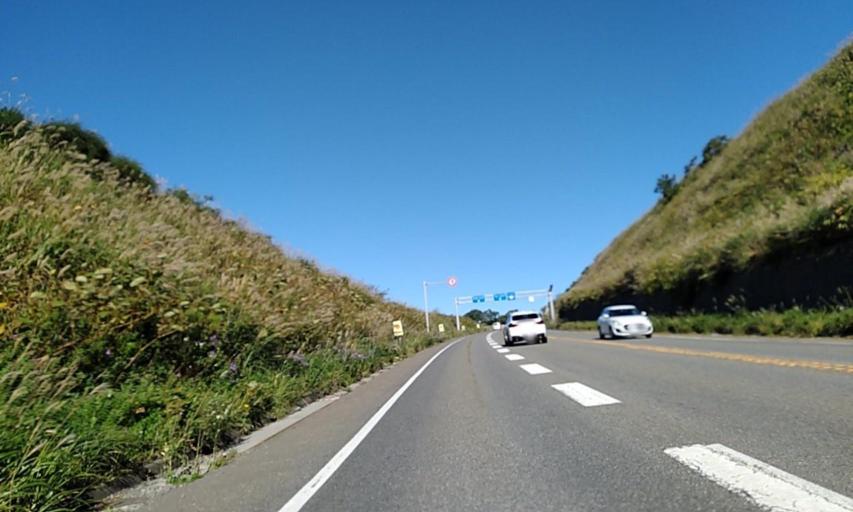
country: JP
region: Hokkaido
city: Shizunai-furukawacho
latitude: 42.3968
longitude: 142.2581
